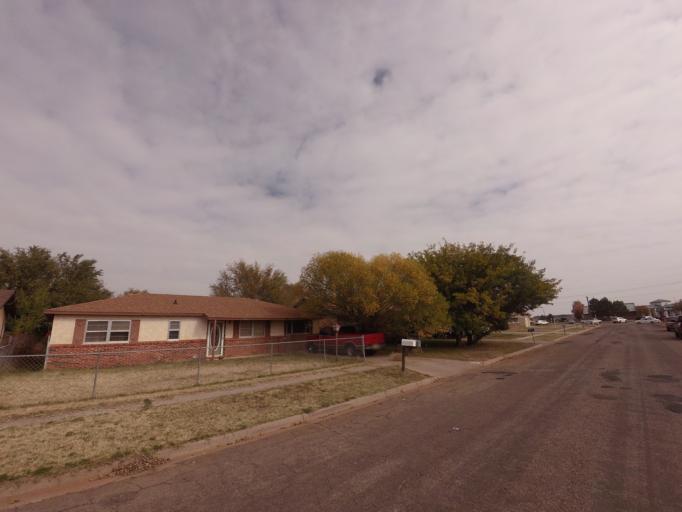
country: US
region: New Mexico
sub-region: Curry County
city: Clovis
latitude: 34.4313
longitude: -103.2153
